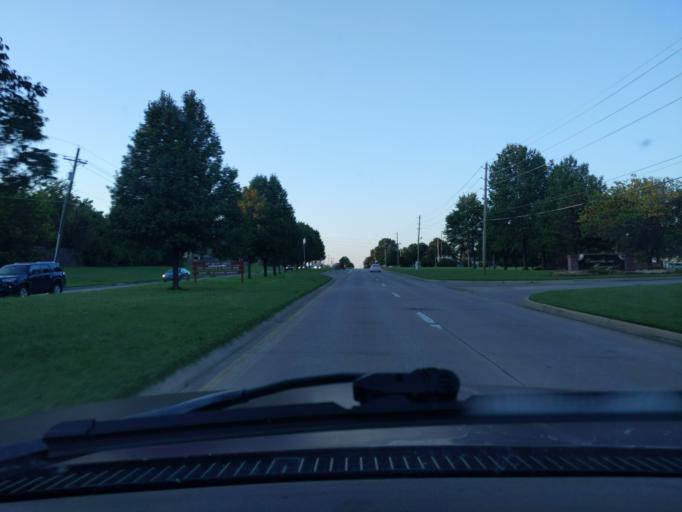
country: US
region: Oklahoma
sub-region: Tulsa County
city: Jenks
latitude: 36.0506
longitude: -95.8861
